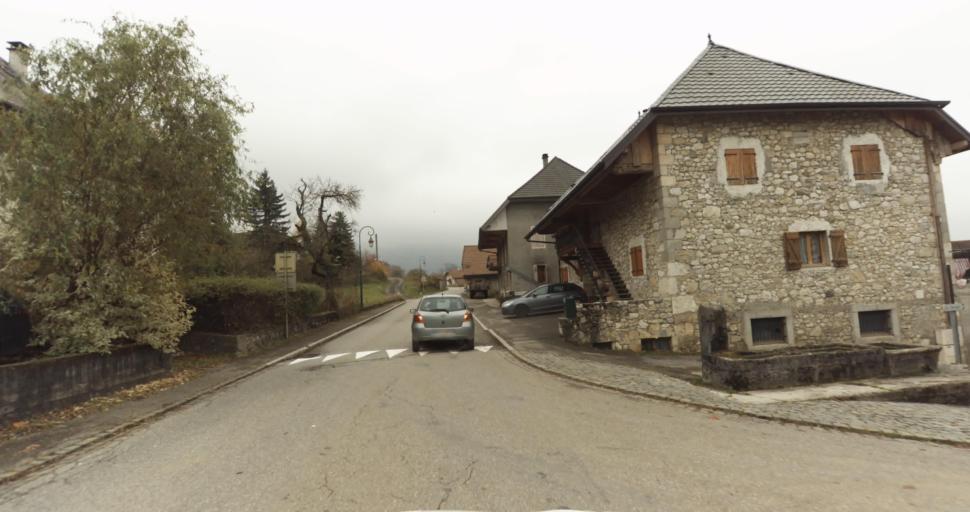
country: FR
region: Rhone-Alpes
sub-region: Departement de la Haute-Savoie
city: Gruffy
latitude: 45.7830
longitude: 6.0532
